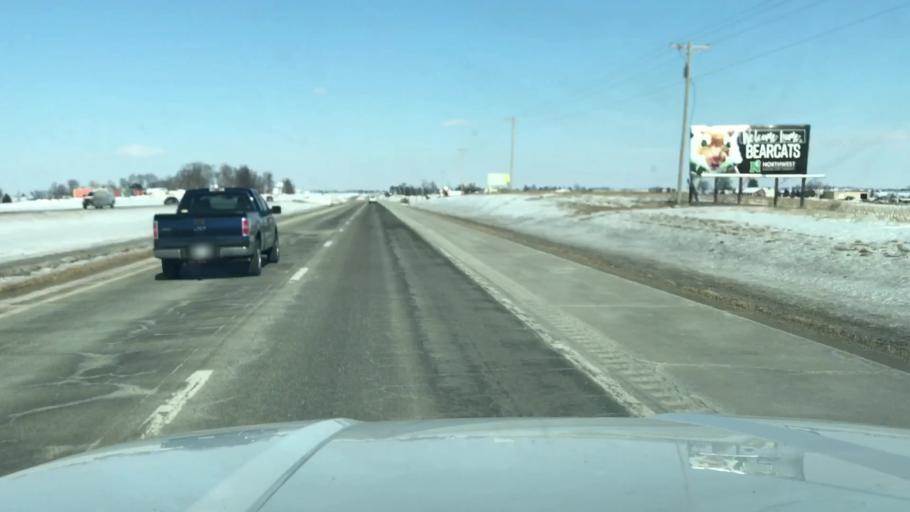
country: US
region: Missouri
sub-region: Nodaway County
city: Maryville
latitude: 40.2846
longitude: -94.8754
